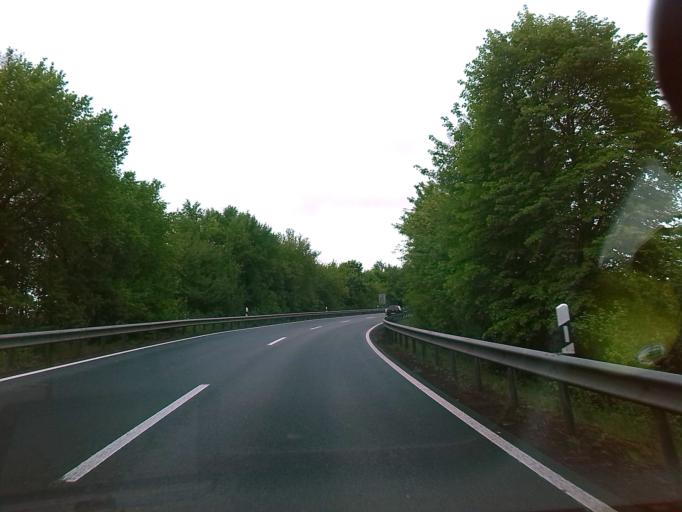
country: DE
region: Rheinland-Pfalz
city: Mutterstadt
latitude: 49.4574
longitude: 8.3604
